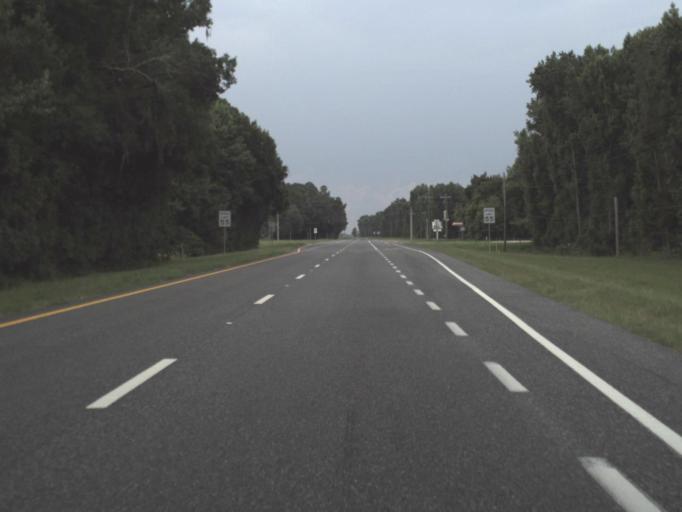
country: US
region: Florida
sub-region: Levy County
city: Williston Highlands
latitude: 29.2552
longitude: -82.7249
